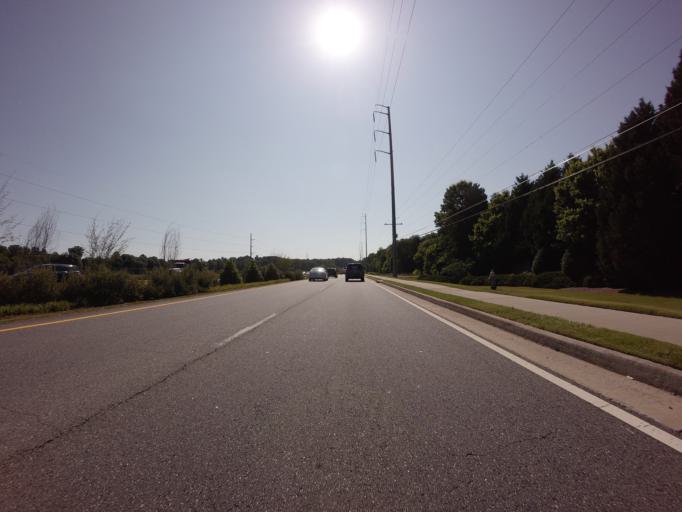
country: US
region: Georgia
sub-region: Gwinnett County
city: Suwanee
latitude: 34.0508
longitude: -84.1063
